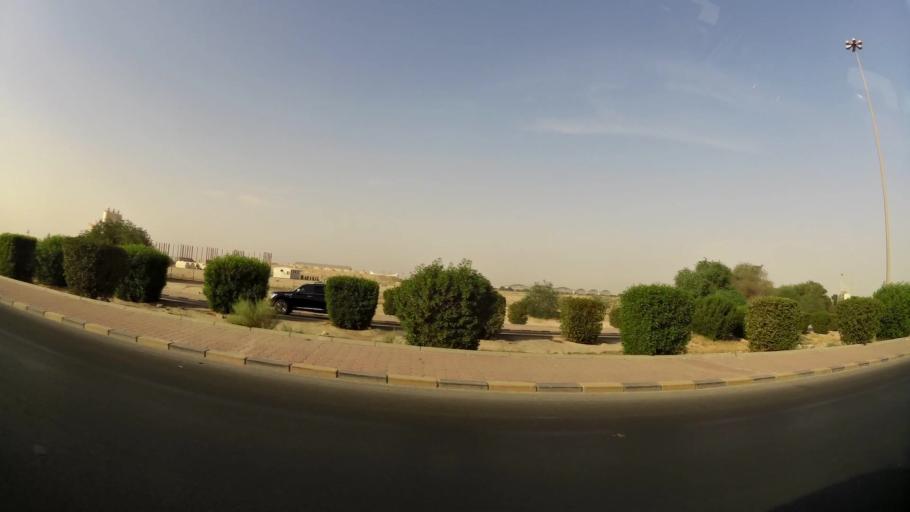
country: KW
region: Al Farwaniyah
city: Janub as Surrah
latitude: 29.2493
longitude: 47.9900
